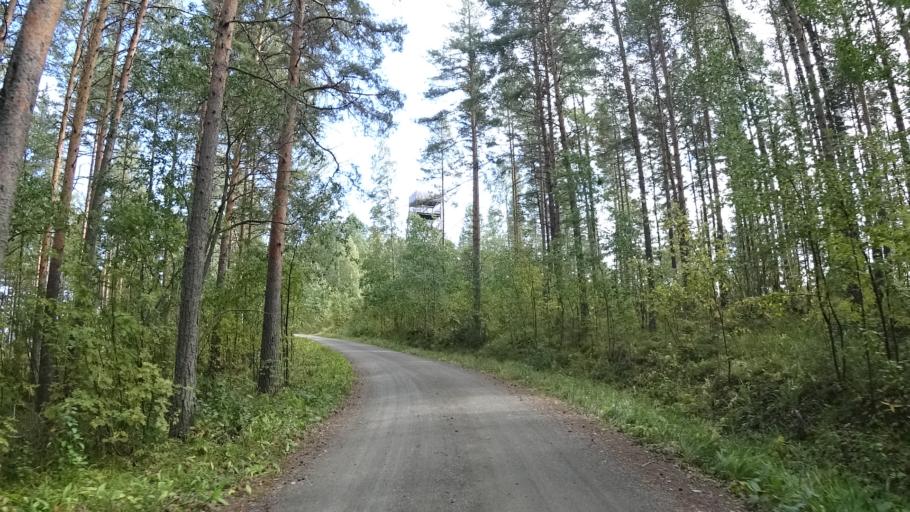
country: FI
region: North Karelia
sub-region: Keski-Karjala
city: Raeaekkylae
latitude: 62.3956
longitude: 29.7611
